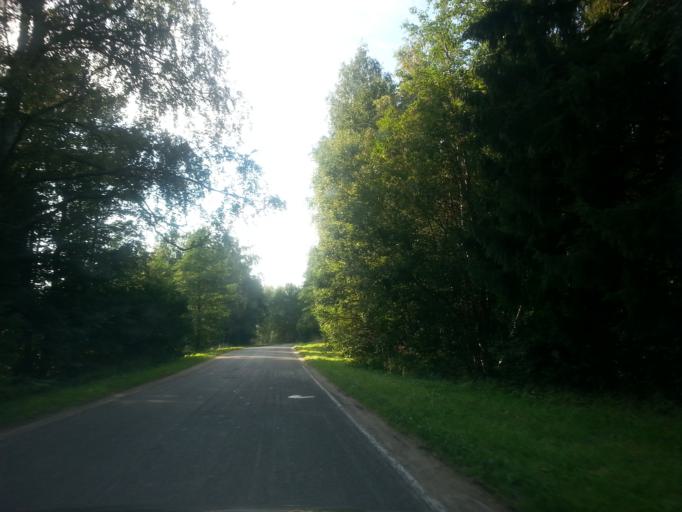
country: BY
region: Minsk
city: Narach
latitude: 54.9629
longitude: 26.6445
